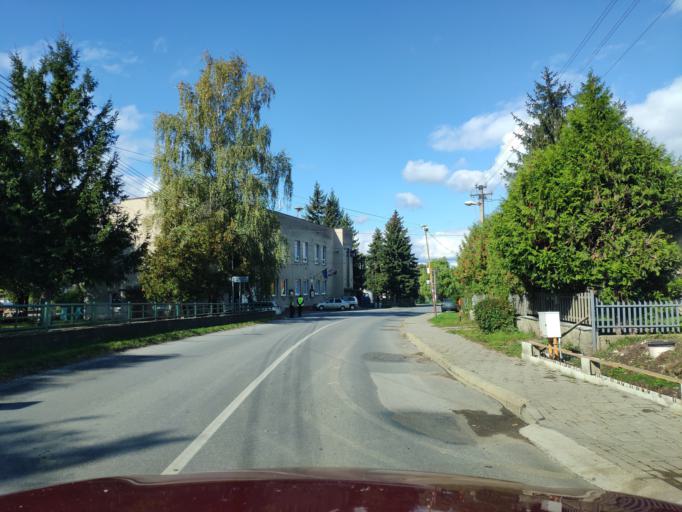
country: SK
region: Presovsky
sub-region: Okres Presov
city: Presov
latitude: 48.9527
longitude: 21.3060
